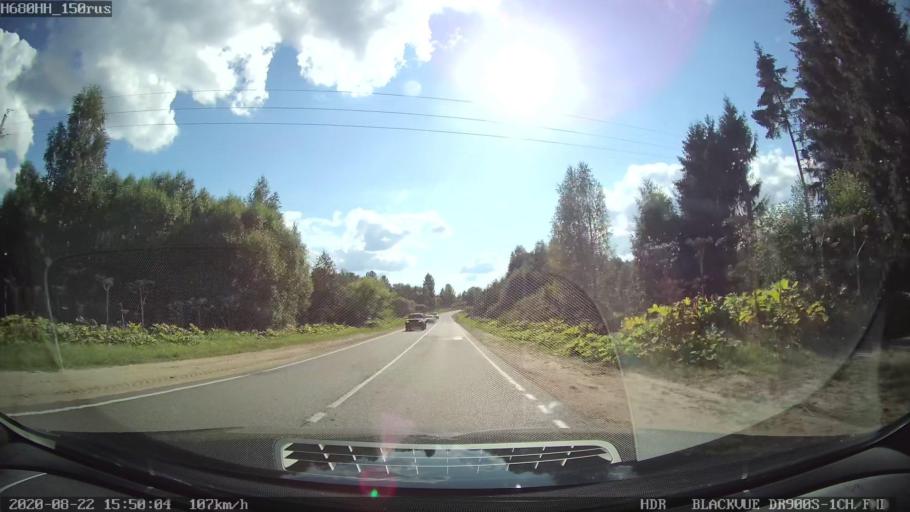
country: RU
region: Tverskaya
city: Bezhetsk
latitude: 57.6726
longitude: 36.4475
